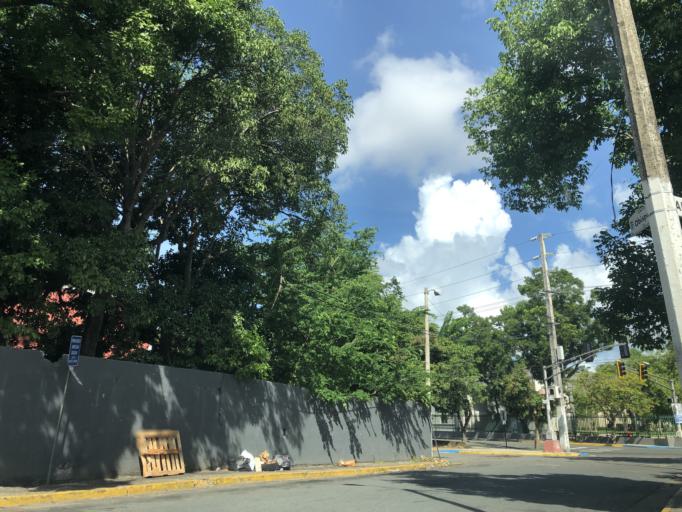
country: PR
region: Trujillo Alto
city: Trujillo Alto
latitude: 18.4010
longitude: -66.0480
